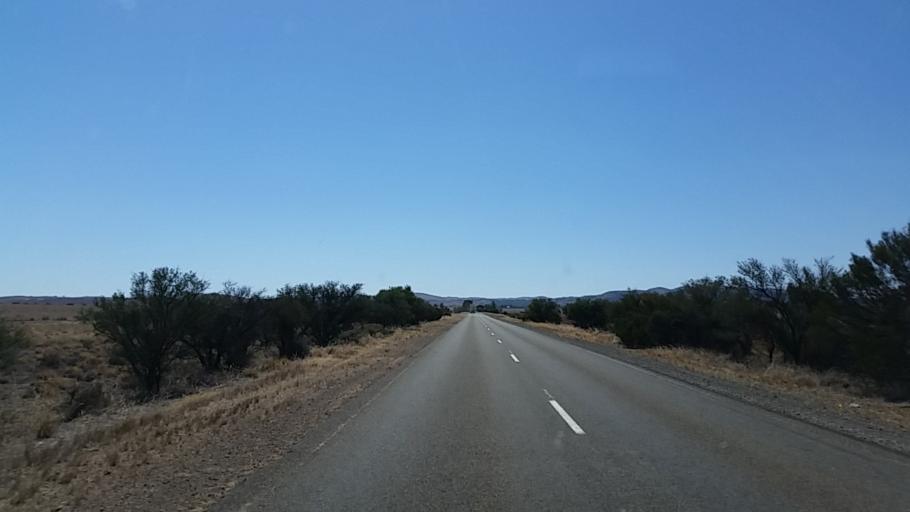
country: AU
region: South Australia
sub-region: Peterborough
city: Peterborough
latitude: -32.6460
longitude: 138.6002
